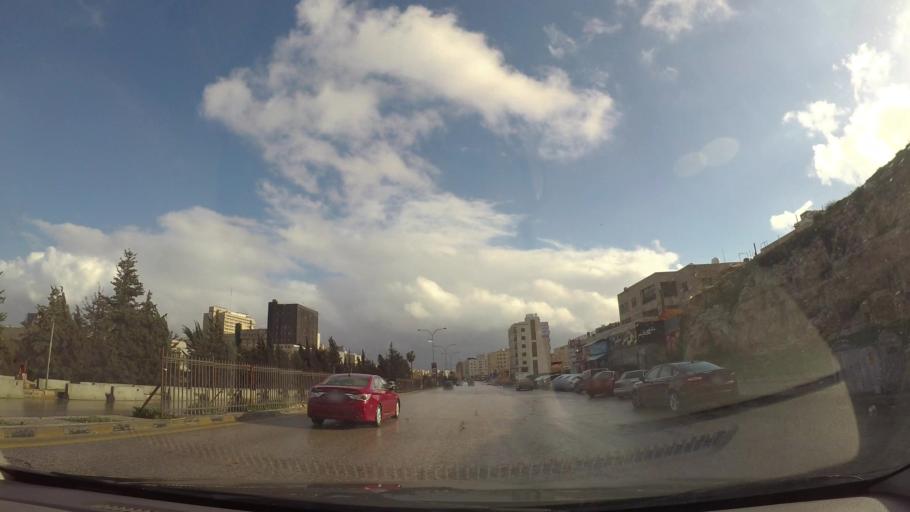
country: JO
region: Amman
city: Al Jubayhah
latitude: 32.0100
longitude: 35.8711
